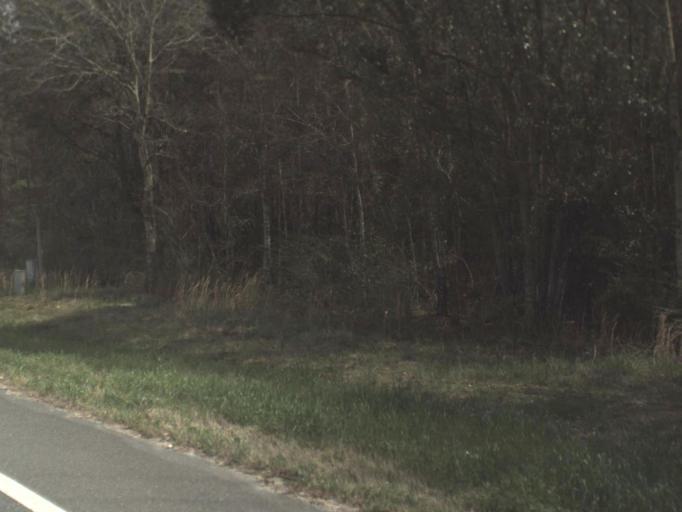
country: US
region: Florida
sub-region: Jackson County
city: Graceville
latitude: 30.9632
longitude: -85.5544
